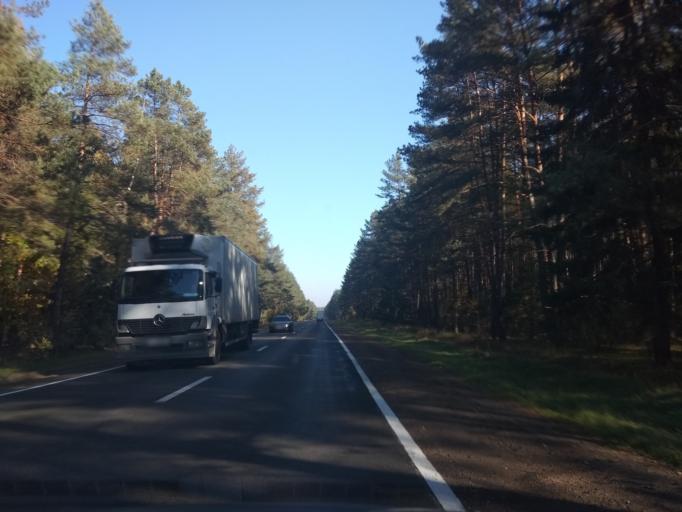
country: BY
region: Brest
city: Baranovichi
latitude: 53.0363
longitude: 25.8051
